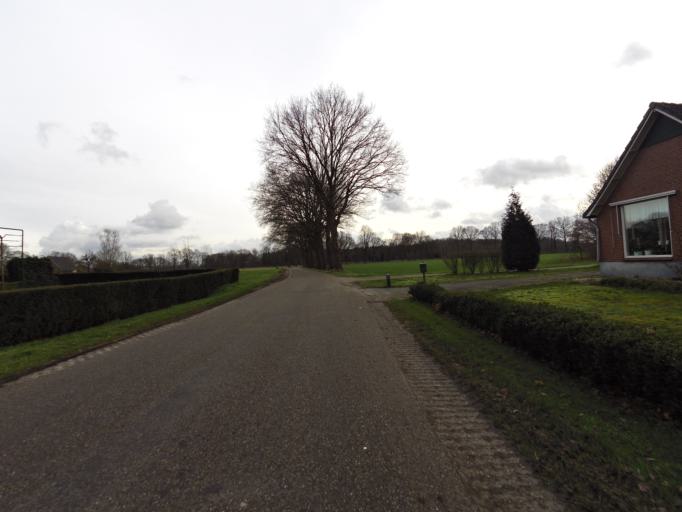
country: NL
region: Gelderland
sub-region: Oude IJsselstreek
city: Wisch
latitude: 51.9428
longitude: 6.4135
